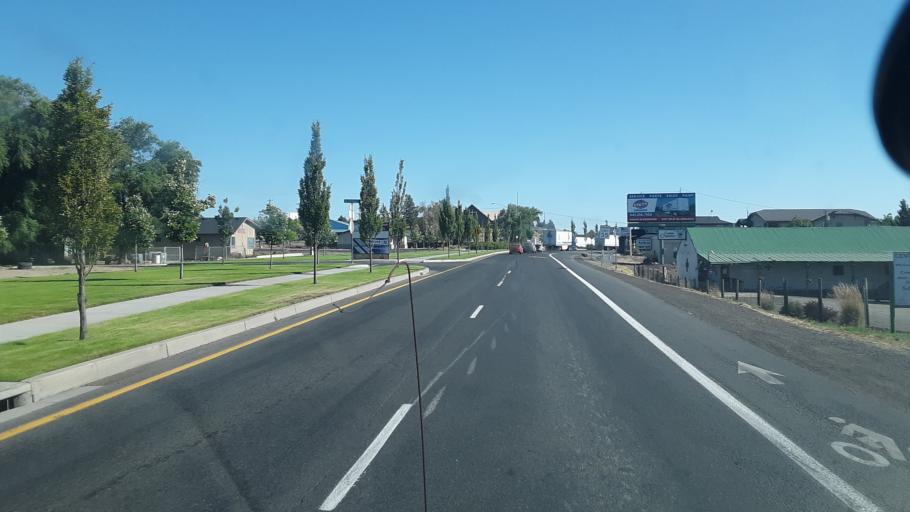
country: US
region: Oregon
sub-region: Jefferson County
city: Madras
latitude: 44.6251
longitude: -121.1306
